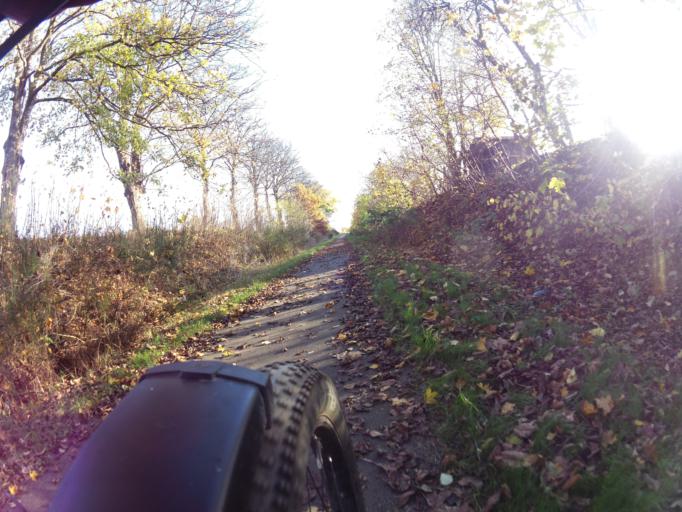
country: PL
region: Pomeranian Voivodeship
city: Strzelno
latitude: 54.7657
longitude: 18.2475
